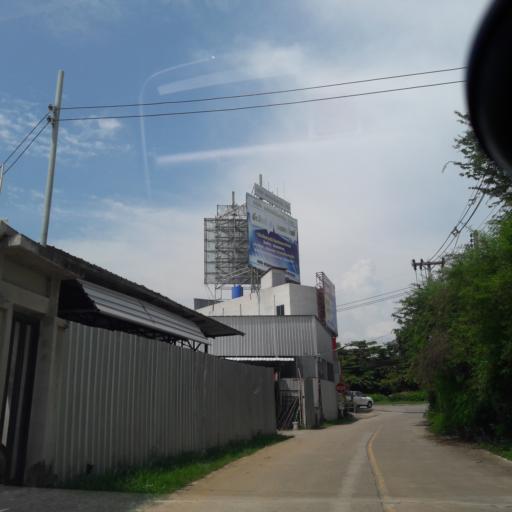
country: TH
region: Chiang Mai
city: San Sai
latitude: 18.8229
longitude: 99.0446
